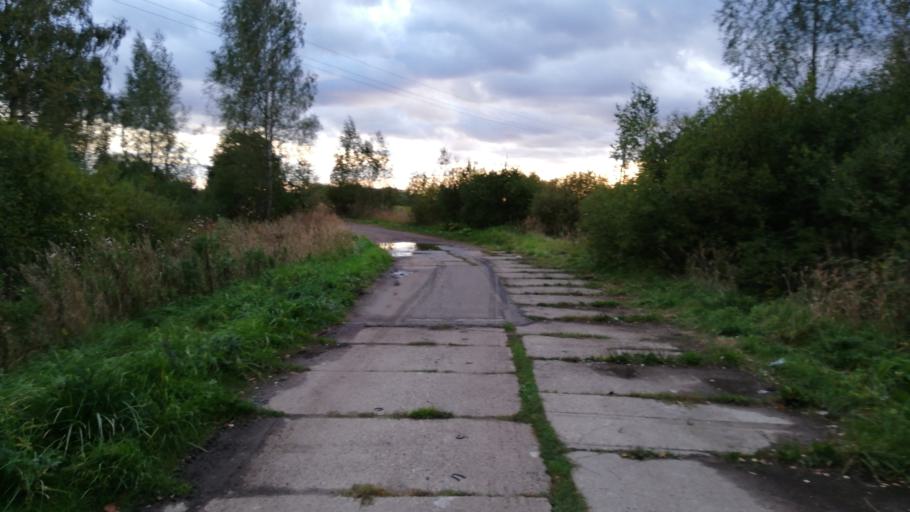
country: RU
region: Ivanovo
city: Pistsovo
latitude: 57.1890
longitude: 40.4428
